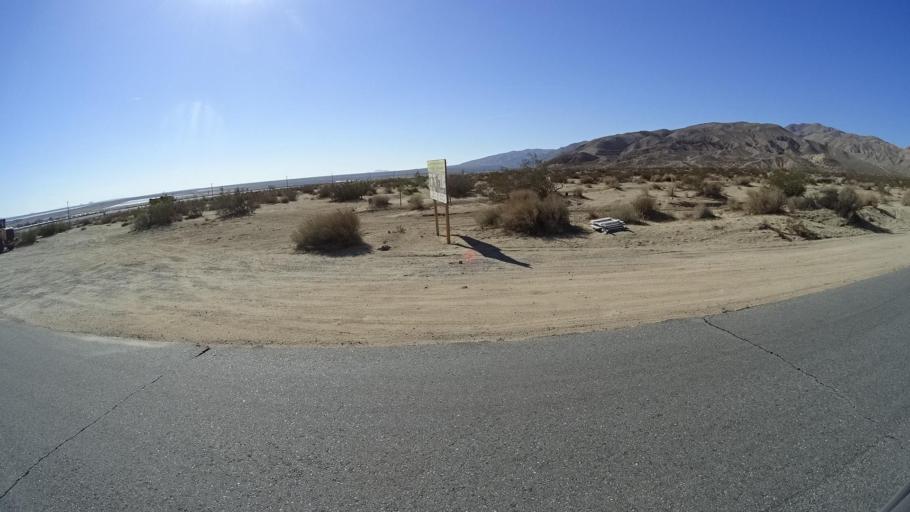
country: US
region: California
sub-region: Kern County
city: California City
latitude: 35.3010
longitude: -118.0014
